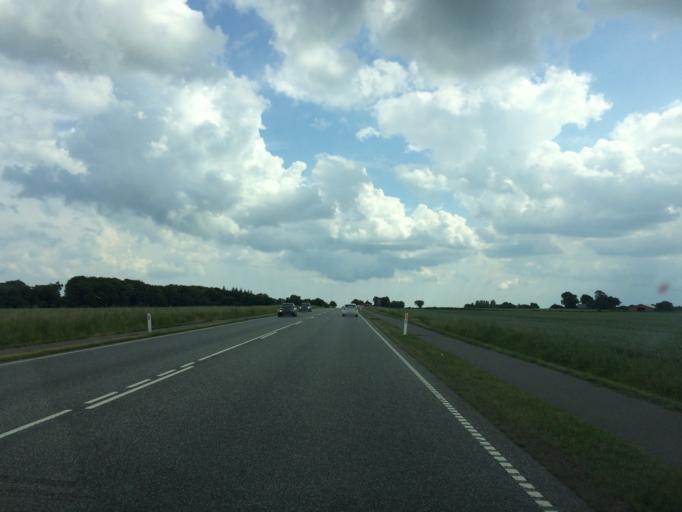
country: DK
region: South Denmark
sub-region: Vejle Kommune
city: Borkop
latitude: 55.6208
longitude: 9.6104
